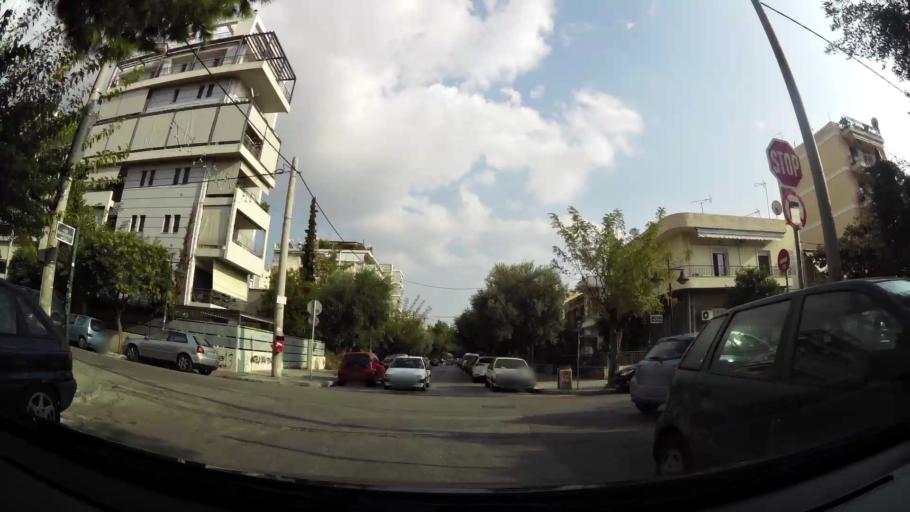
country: GR
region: Attica
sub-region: Nomarchia Athinas
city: Moskhaton
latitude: 37.9426
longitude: 23.6873
